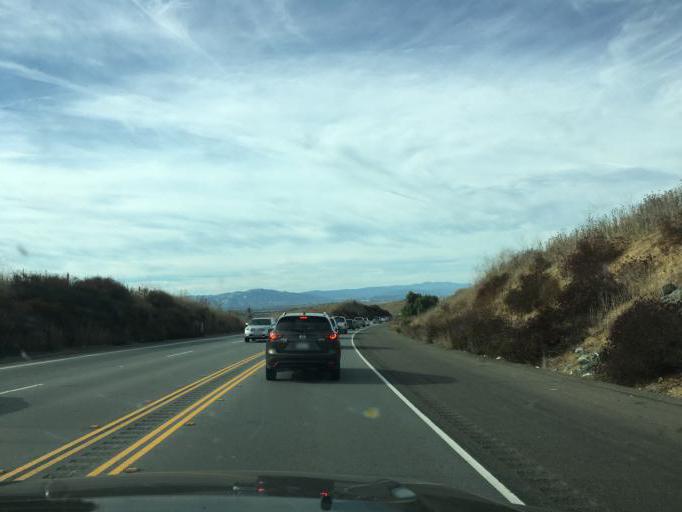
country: US
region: California
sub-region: San Benito County
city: Hollister
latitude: 36.9611
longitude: -121.4023
